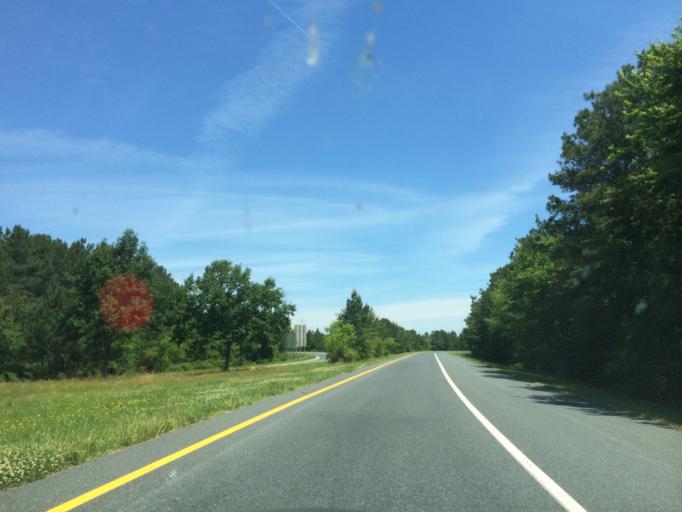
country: US
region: Maryland
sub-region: Wicomico County
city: Salisbury
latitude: 38.3317
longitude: -75.5674
